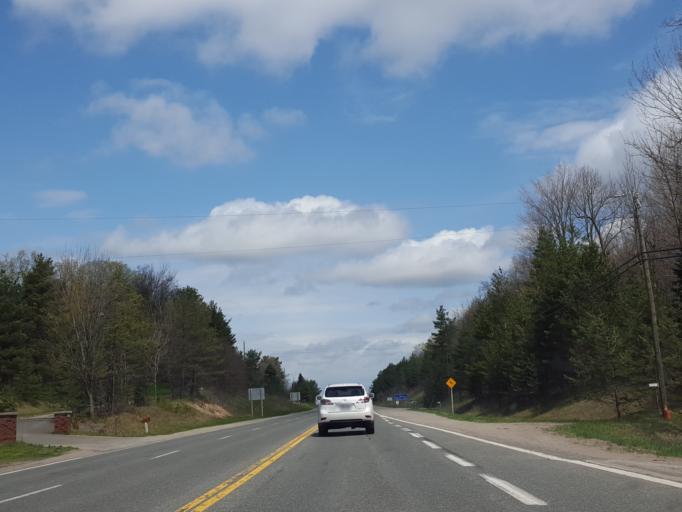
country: CA
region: Ontario
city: Newmarket
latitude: 44.0956
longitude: -79.3105
